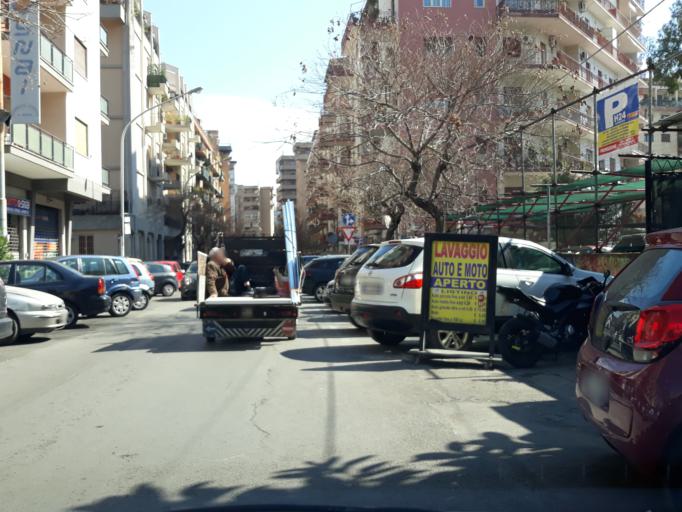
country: IT
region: Sicily
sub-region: Palermo
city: Palermo
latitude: 38.1381
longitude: 13.3507
